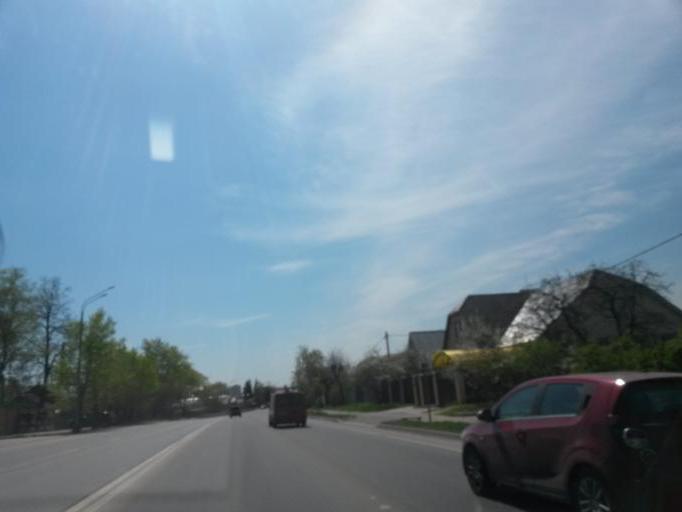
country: RU
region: Moskovskaya
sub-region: Podol'skiy Rayon
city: Podol'sk
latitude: 55.4007
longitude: 37.5513
